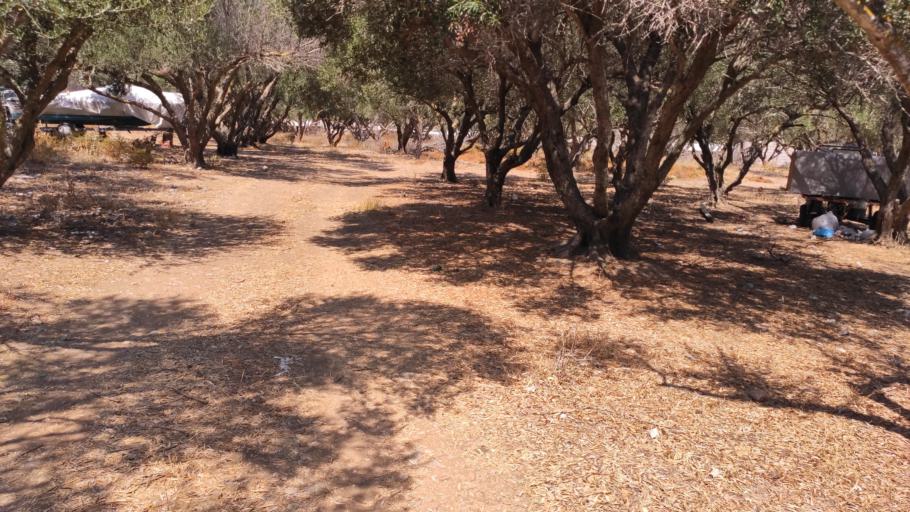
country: GR
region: South Aegean
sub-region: Nomos Dodekanisou
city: Pylion
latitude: 36.9334
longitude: 27.1354
